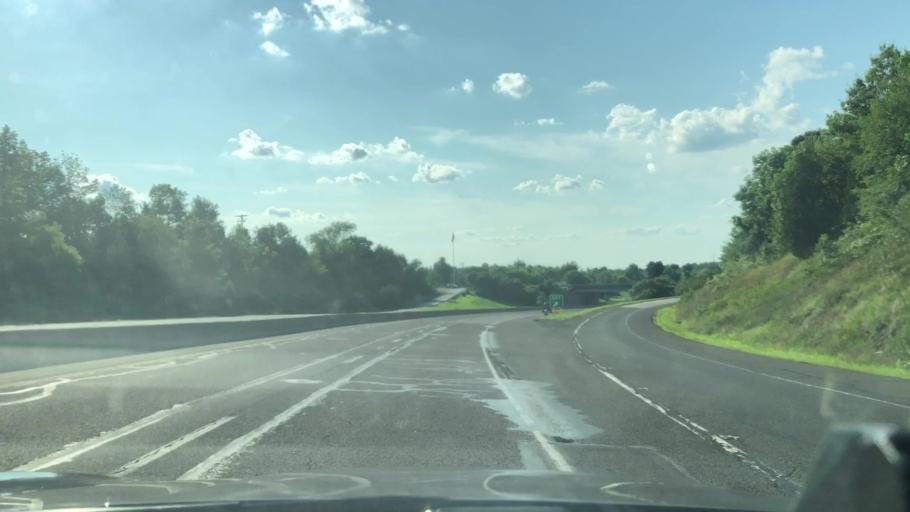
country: US
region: Pennsylvania
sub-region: Montgomery County
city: Souderton
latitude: 40.3155
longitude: -75.3057
